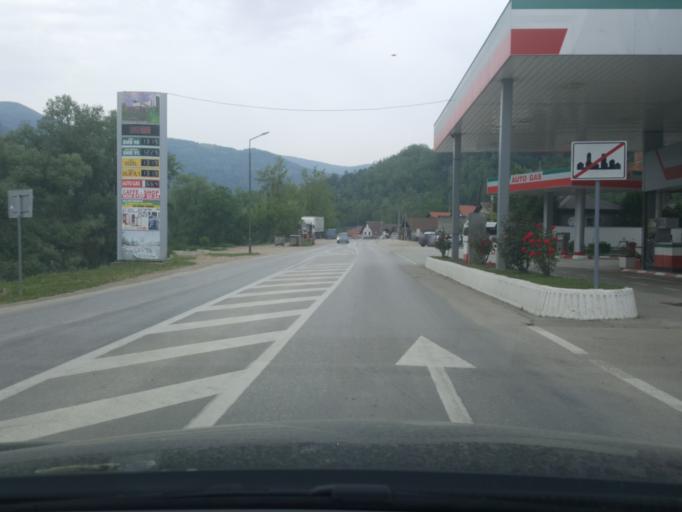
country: RS
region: Central Serbia
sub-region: Zlatiborski Okrug
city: Bajina Basta
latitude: 43.9857
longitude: 19.5687
